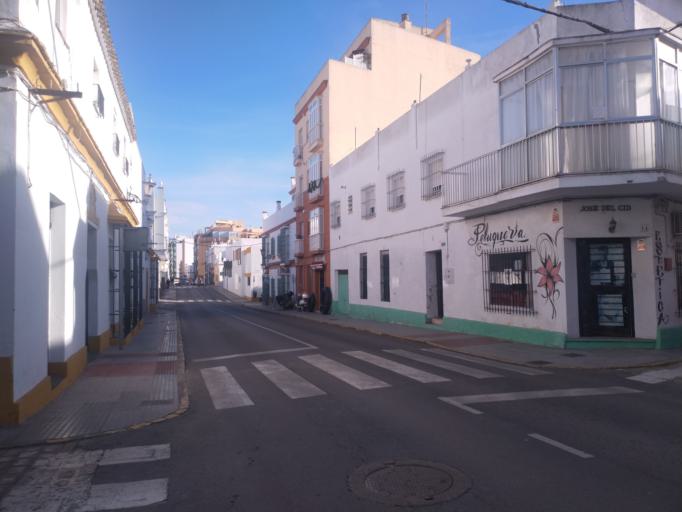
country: ES
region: Andalusia
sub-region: Provincia de Cadiz
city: San Fernando
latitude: 36.4715
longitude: -6.1969
